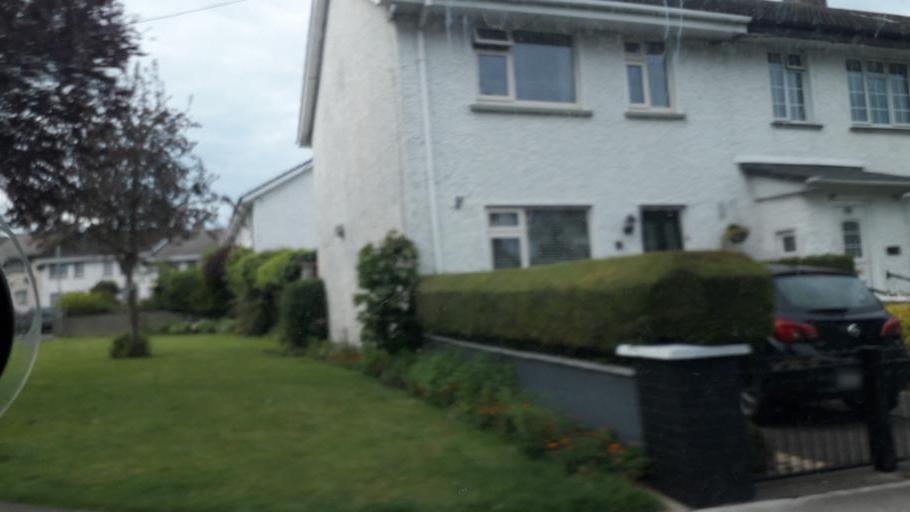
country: IE
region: Leinster
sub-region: Kildare
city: Celbridge
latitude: 53.3391
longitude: -6.5422
